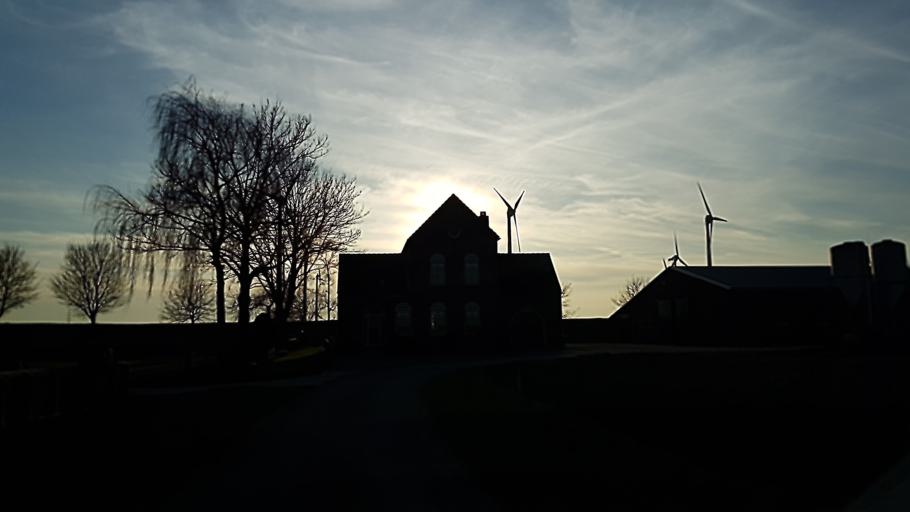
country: NL
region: North Brabant
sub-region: Gemeente Woensdrecht
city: Woensdrecht
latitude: 51.3827
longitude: 4.2758
